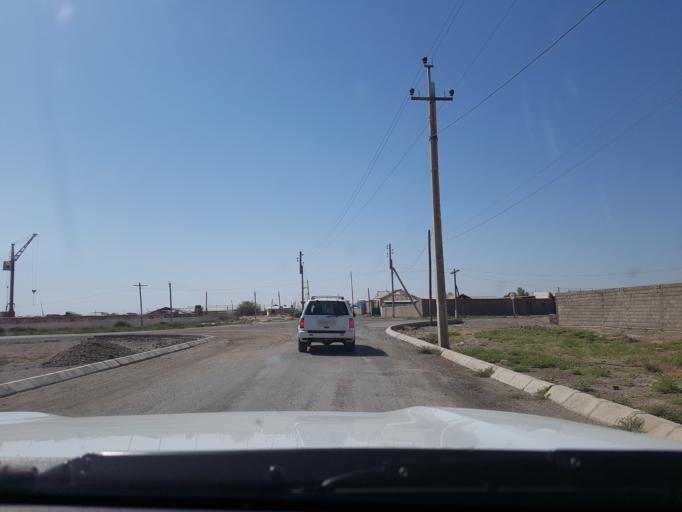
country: IR
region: Razavi Khorasan
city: Sarakhs
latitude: 36.5134
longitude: 61.2233
